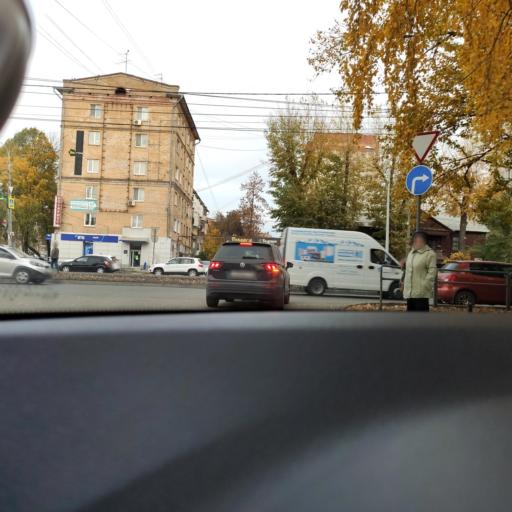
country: RU
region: Samara
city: Samara
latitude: 53.1998
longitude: 50.1778
